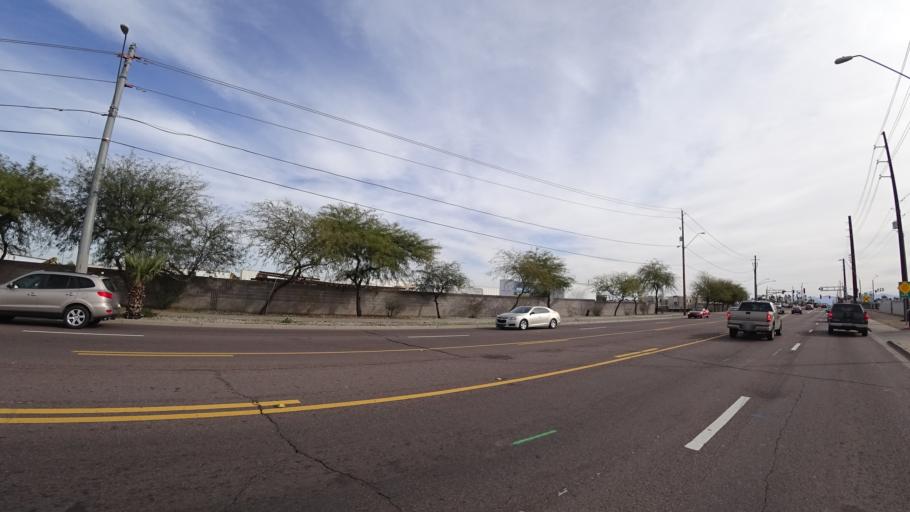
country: US
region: Arizona
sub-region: Maricopa County
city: Sun City
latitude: 33.5943
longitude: -112.2552
